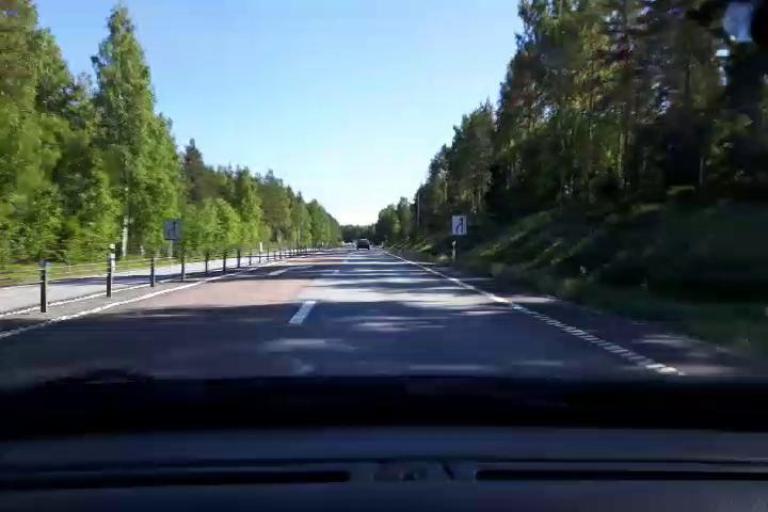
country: SE
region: Gaevleborg
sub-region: Gavle Kommun
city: Norrsundet
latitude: 61.0127
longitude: 16.9812
